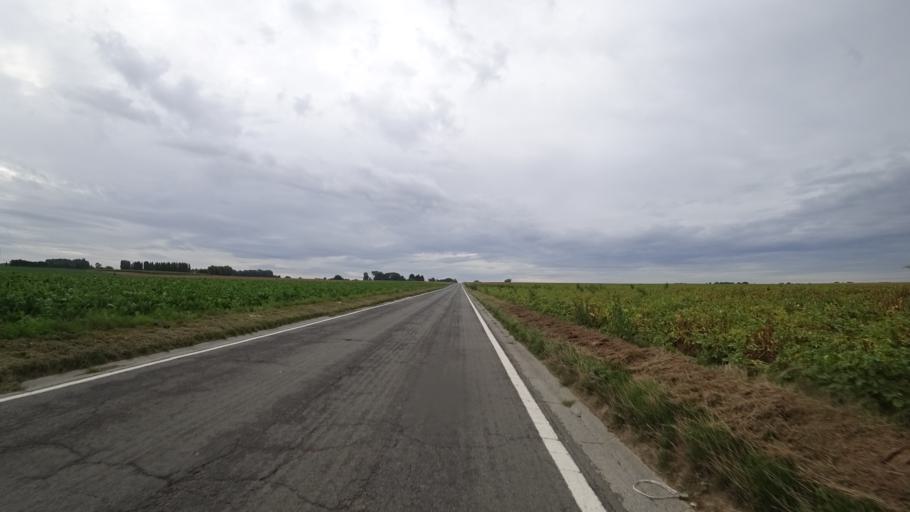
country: BE
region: Wallonia
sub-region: Province du Brabant Wallon
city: Perwez
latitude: 50.5926
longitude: 4.7582
